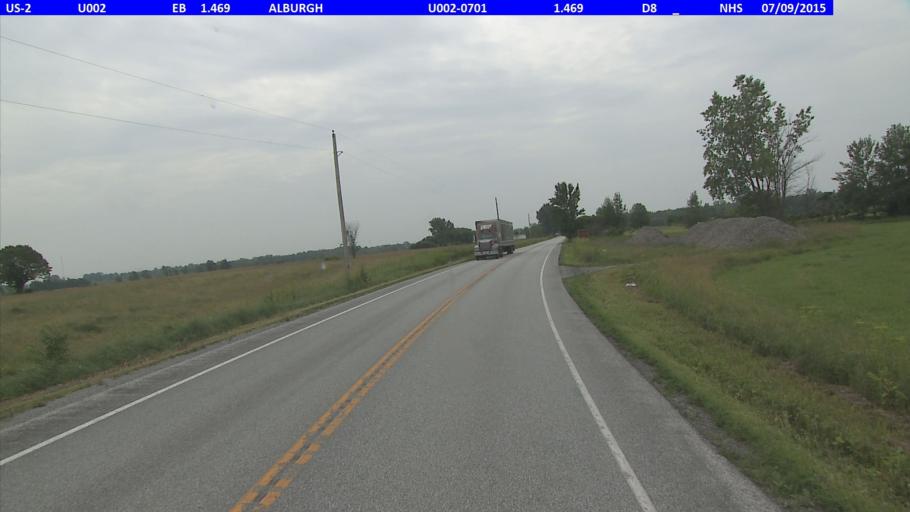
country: US
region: New York
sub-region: Clinton County
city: Rouses Point
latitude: 44.9974
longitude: -73.3208
